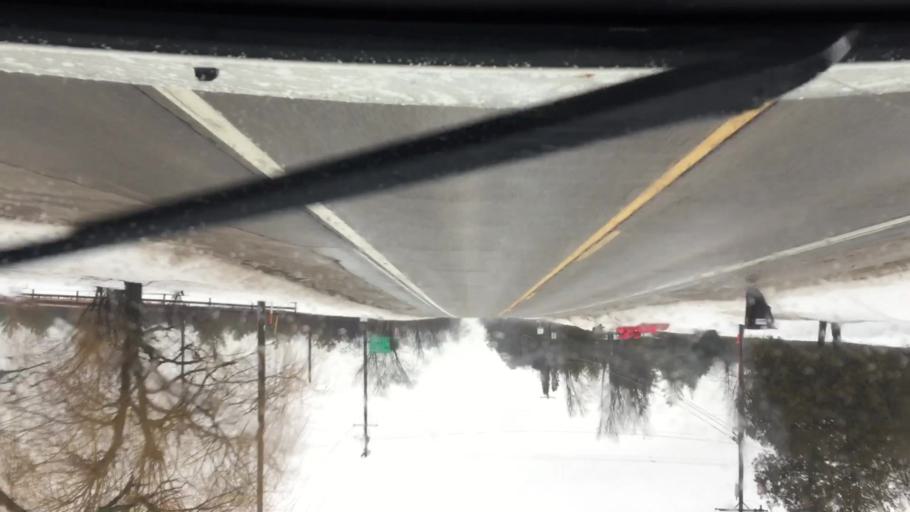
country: US
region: Michigan
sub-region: Charlevoix County
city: East Jordan
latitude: 45.1390
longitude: -85.1397
